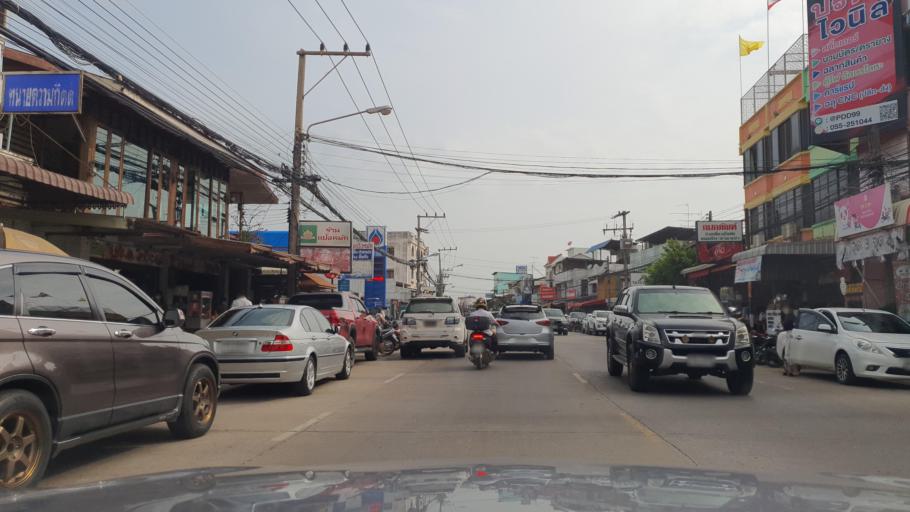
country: TH
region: Phitsanulok
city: Phitsanulok
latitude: 16.8274
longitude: 100.2653
